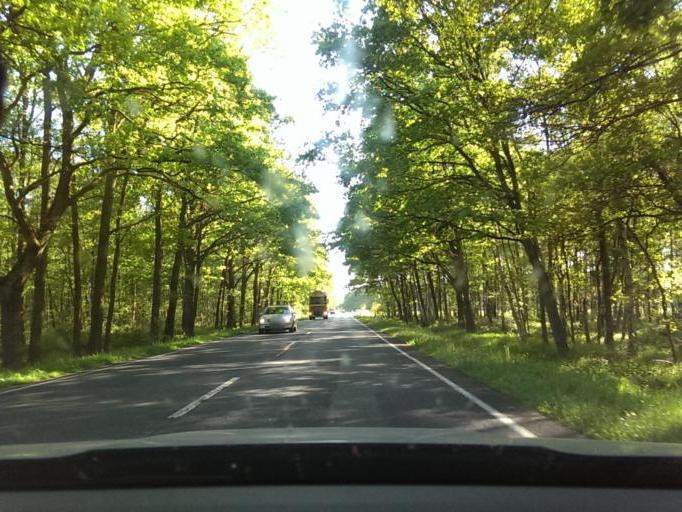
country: DE
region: Lower Saxony
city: Wietze
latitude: 52.5782
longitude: 9.8675
